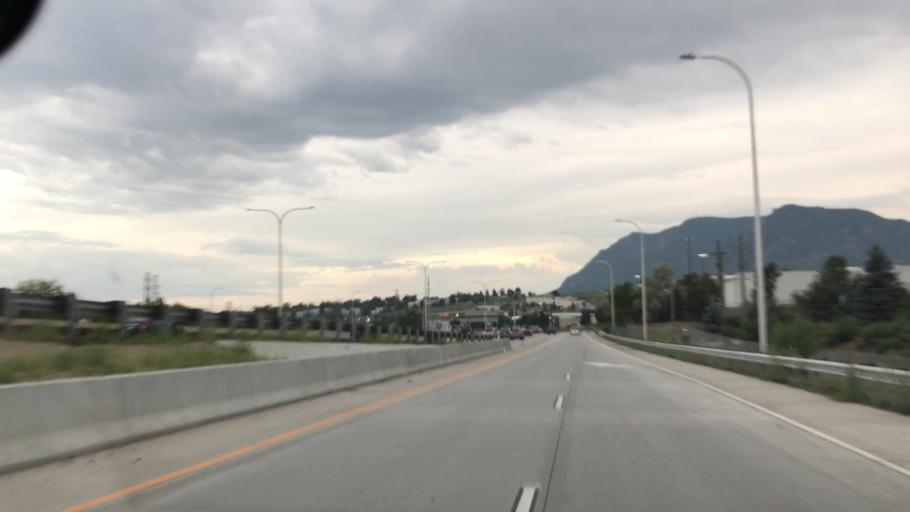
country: US
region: Colorado
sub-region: El Paso County
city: Colorado Springs
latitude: 38.8259
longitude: -104.8362
